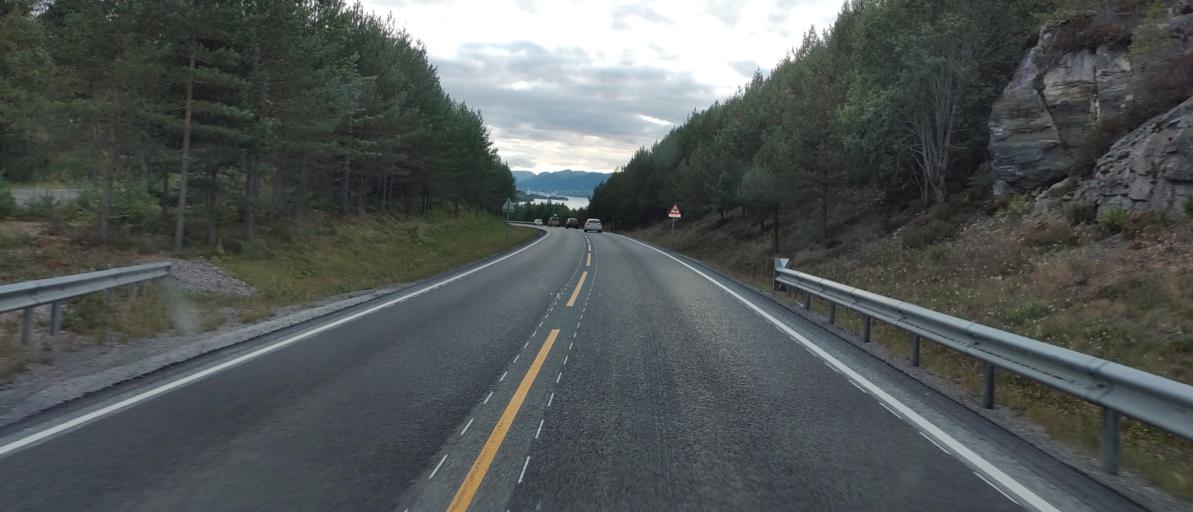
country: NO
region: More og Romsdal
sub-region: Molde
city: Hjelset
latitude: 62.7350
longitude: 7.3910
